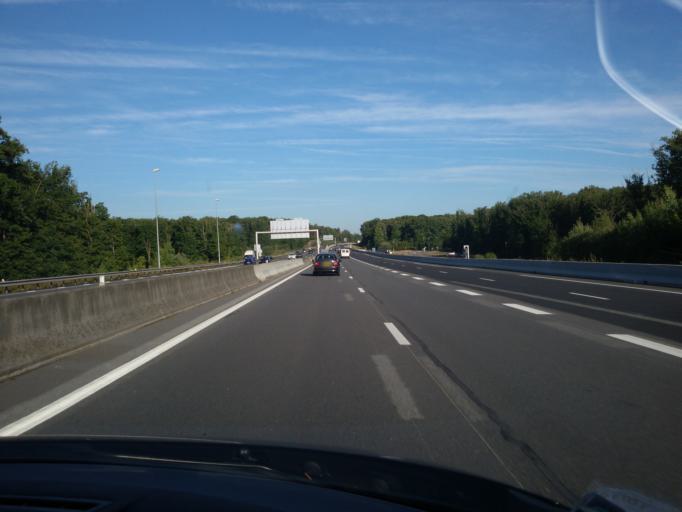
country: FR
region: Centre
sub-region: Departement du Cher
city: Vierzon
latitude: 47.2463
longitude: 2.0653
